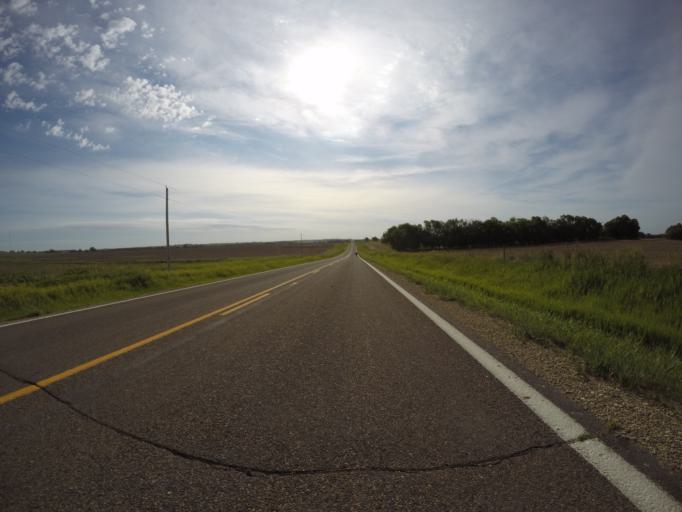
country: US
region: Kansas
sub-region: Republic County
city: Belleville
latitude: 39.7120
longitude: -97.3793
